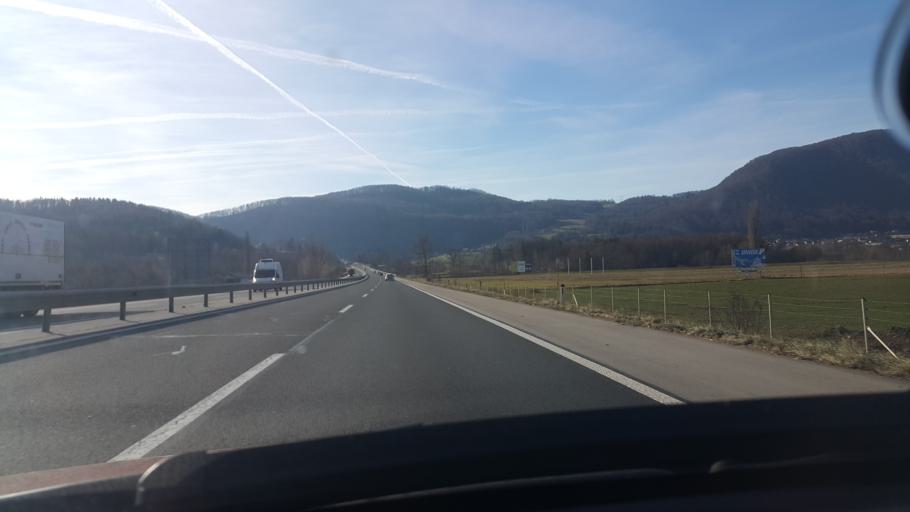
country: SI
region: Slovenska Konjice
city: Slovenske Konjice
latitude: 46.3326
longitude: 15.4700
